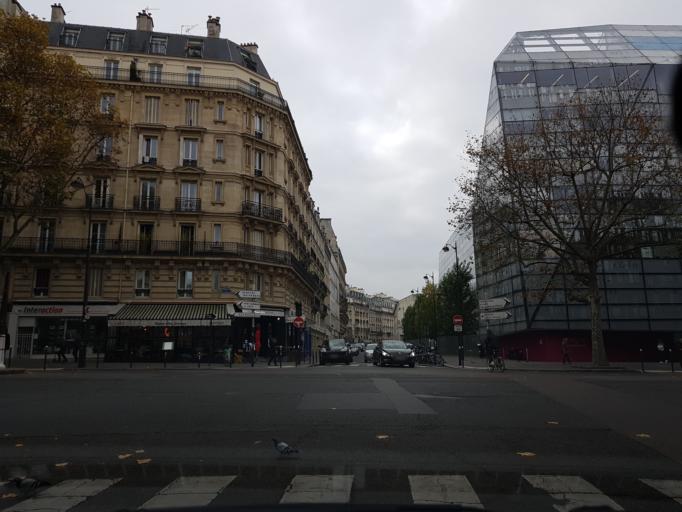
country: FR
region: Ile-de-France
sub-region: Departement des Hauts-de-Seine
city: Montrouge
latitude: 48.8456
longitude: 2.3193
